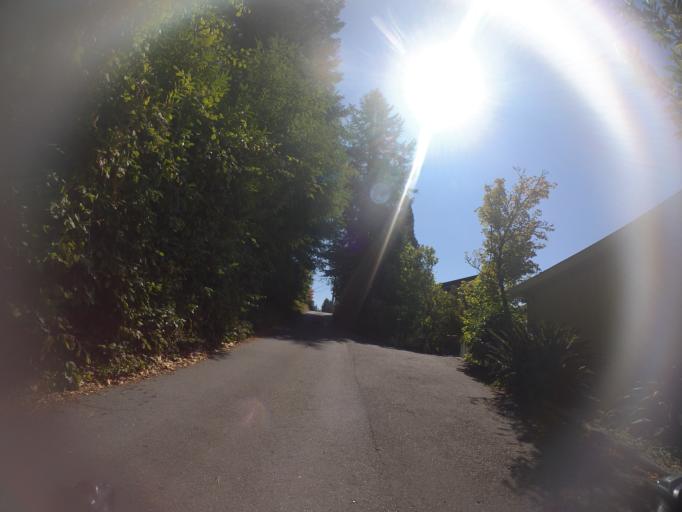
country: US
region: Washington
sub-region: Pierce County
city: University Place
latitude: 47.2180
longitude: -122.5689
